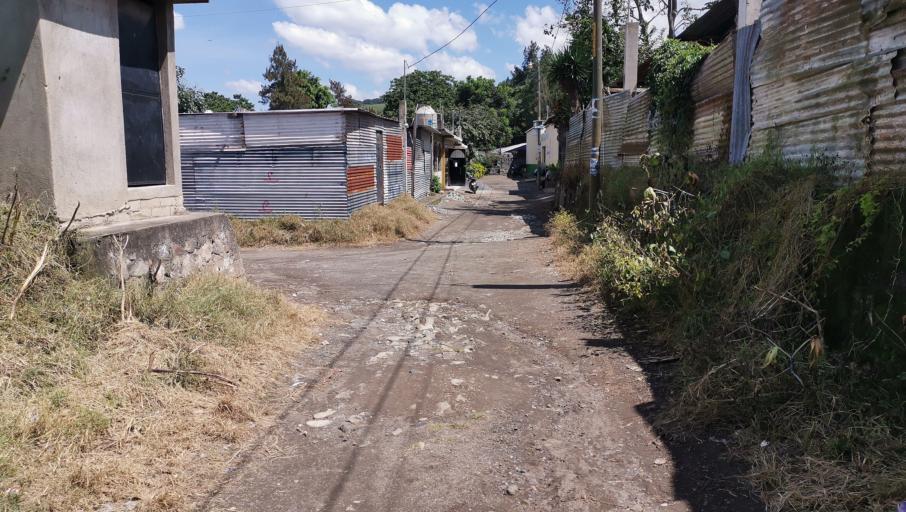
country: GT
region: Escuintla
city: San Vicente Pacaya
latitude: 14.4438
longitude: -90.6316
